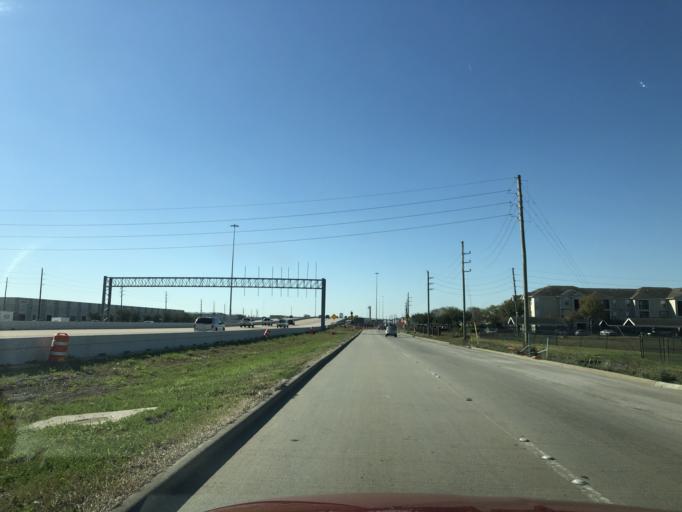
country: US
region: Texas
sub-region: Brazoria County
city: Brookside Village
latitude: 29.5984
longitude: -95.3625
